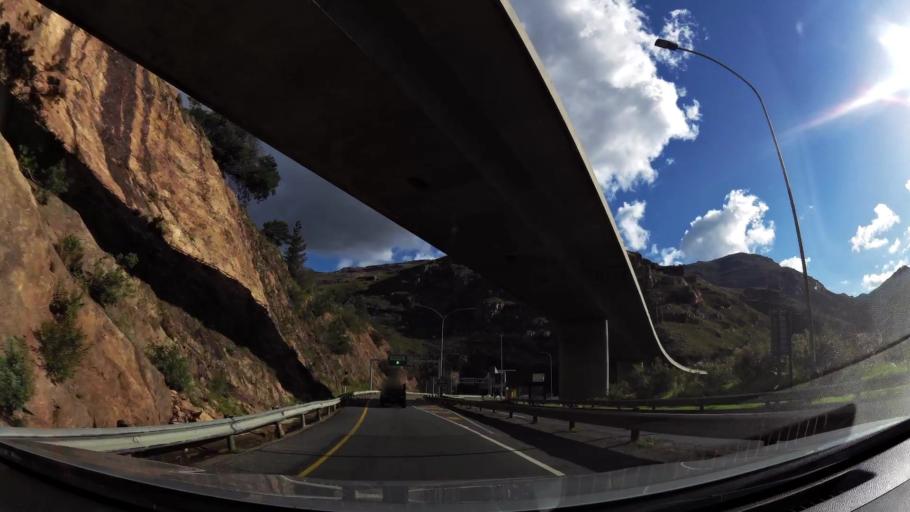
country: ZA
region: Western Cape
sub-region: Cape Winelands District Municipality
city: Paarl
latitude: -33.7319
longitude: 19.1162
